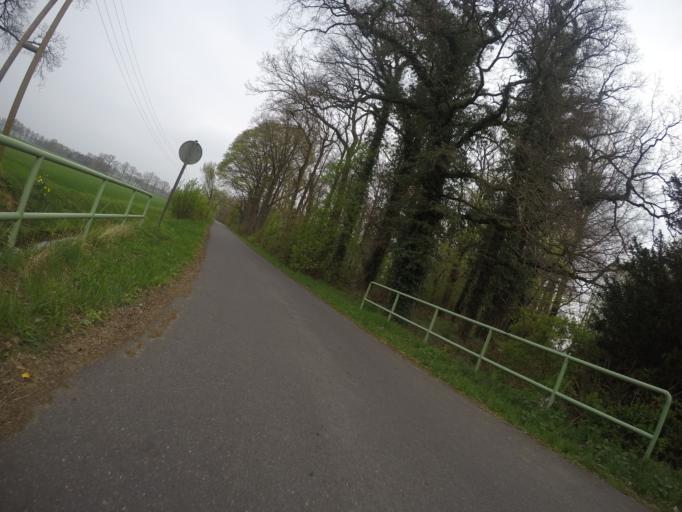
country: NL
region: Gelderland
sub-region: Gemeente Aalten
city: Aalten
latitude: 51.8814
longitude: 6.5643
